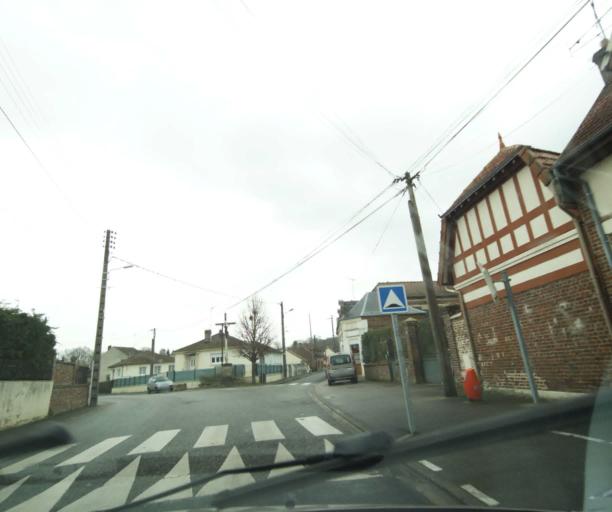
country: FR
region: Picardie
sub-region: Departement de l'Oise
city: Noyon
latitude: 49.5883
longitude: 3.0103
